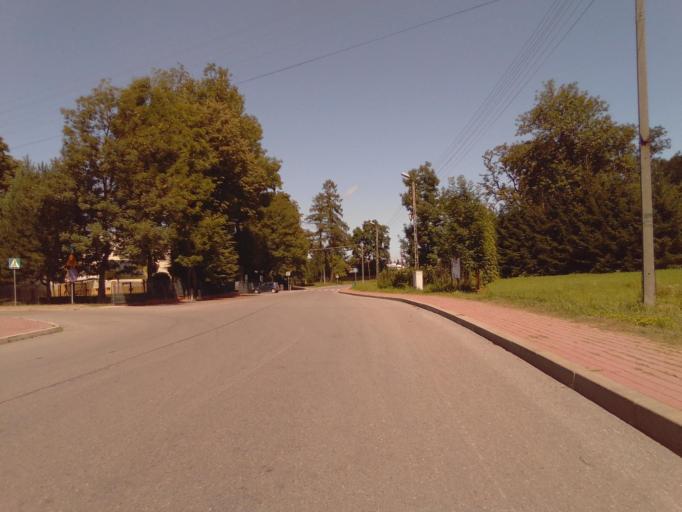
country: PL
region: Subcarpathian Voivodeship
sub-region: Powiat krosnienski
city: Jedlicze
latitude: 49.7144
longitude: 21.6379
